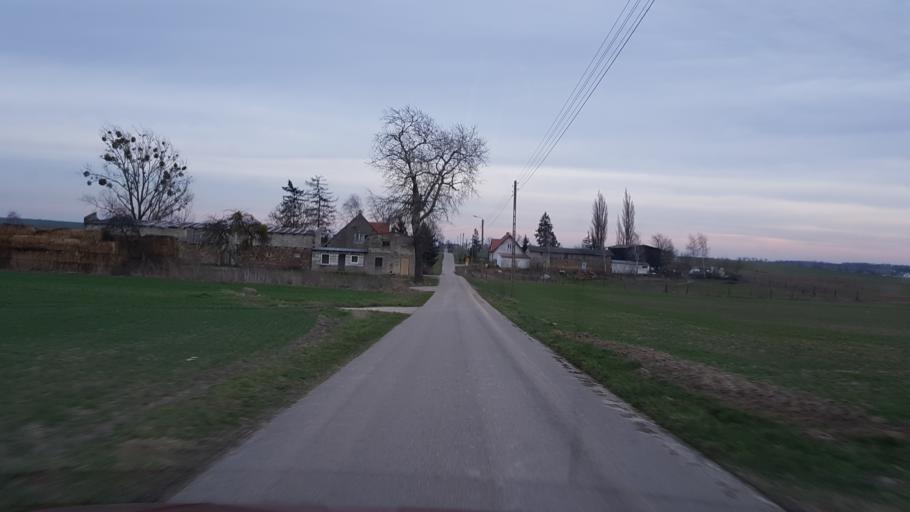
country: PL
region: West Pomeranian Voivodeship
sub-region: Powiat choszczenski
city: Pelczyce
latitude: 53.0320
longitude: 15.2700
